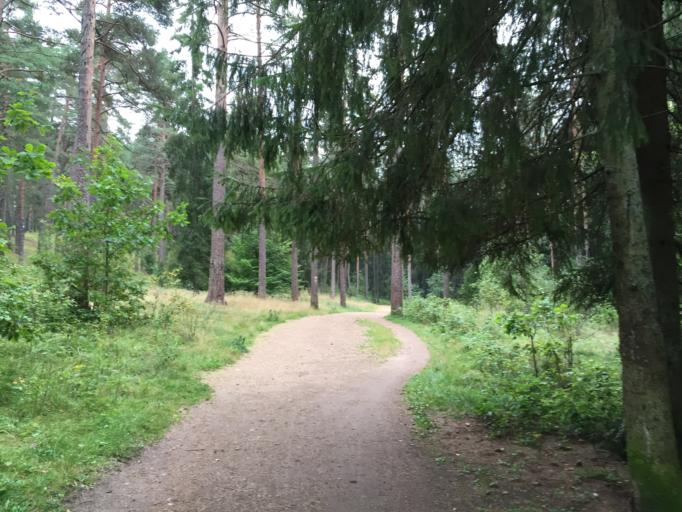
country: LV
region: Ogre
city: Ogre
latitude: 56.8282
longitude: 24.5896
